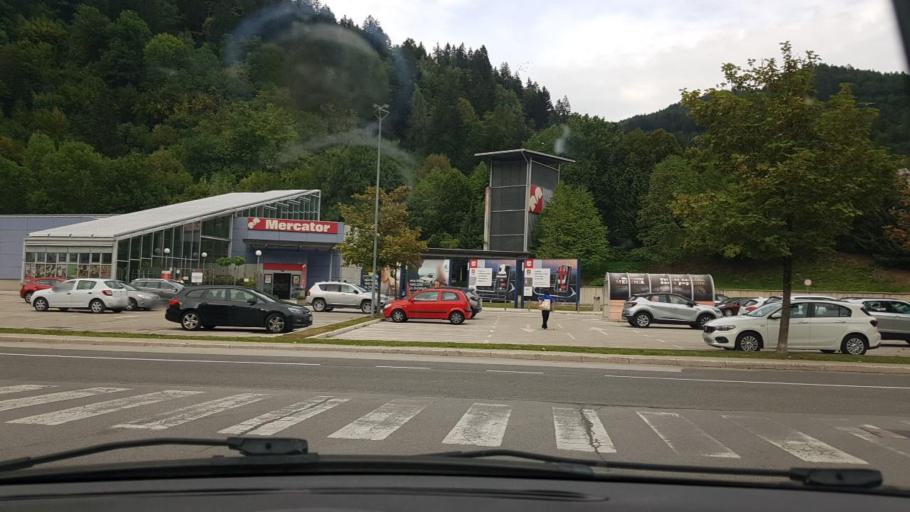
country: SI
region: Jesenice
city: Hrusica
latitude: 46.4417
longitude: 14.0350
